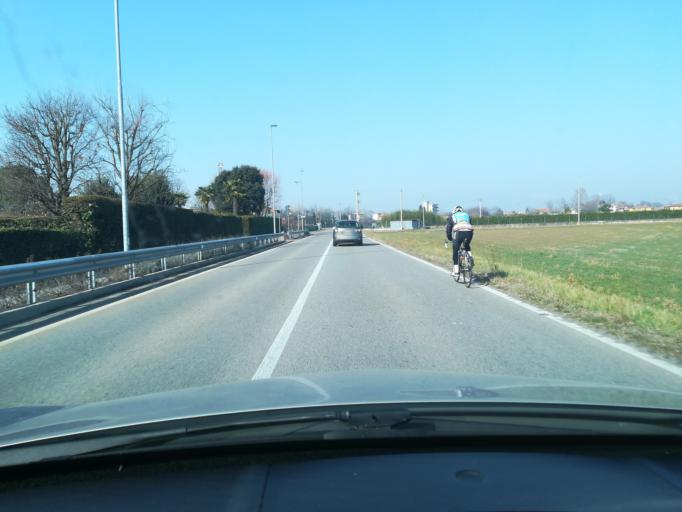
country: IT
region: Lombardy
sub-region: Provincia di Bergamo
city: Zanica
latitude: 45.6453
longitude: 9.6880
